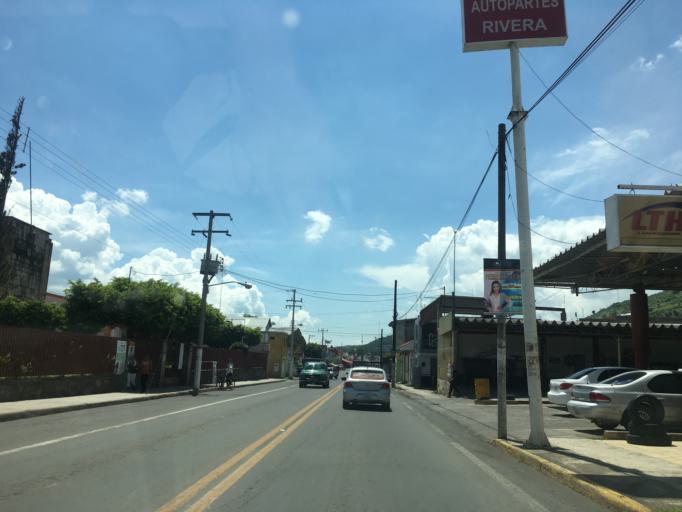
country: MX
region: Nayarit
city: Ixtlan del Rio
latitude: 21.0363
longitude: -104.3754
